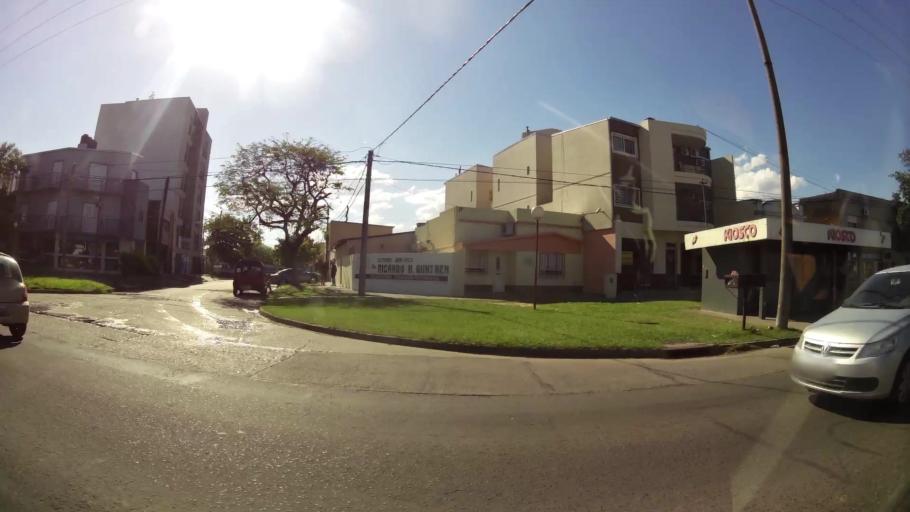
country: AR
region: Santa Fe
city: Santa Fe de la Vera Cruz
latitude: -31.6156
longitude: -60.6824
